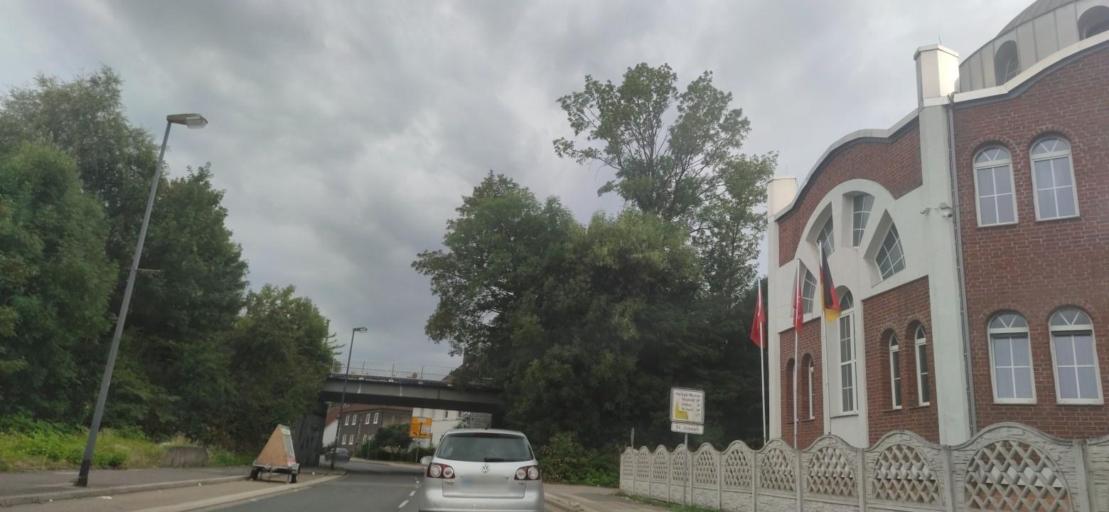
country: DE
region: North Rhine-Westphalia
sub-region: Regierungsbezirk Dusseldorf
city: Essen
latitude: 51.5054
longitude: 7.0490
